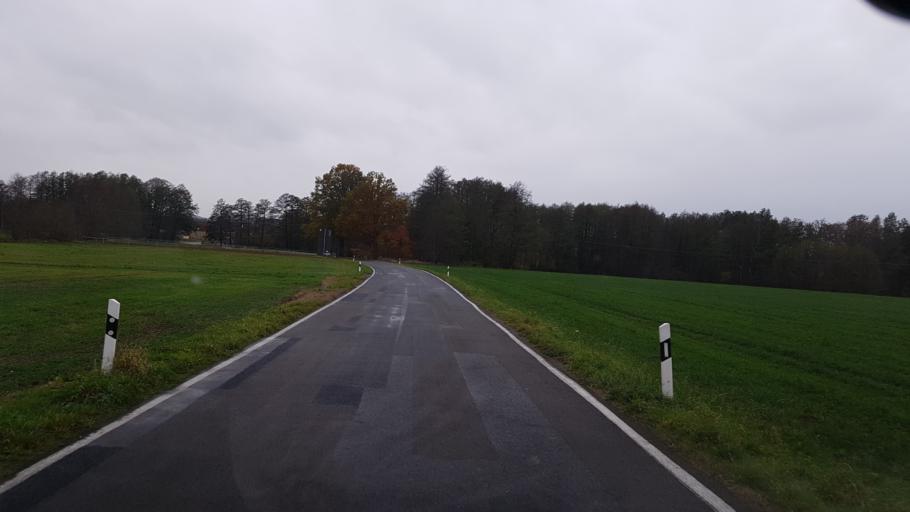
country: DE
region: Brandenburg
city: Ortrand
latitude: 51.3627
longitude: 13.7649
